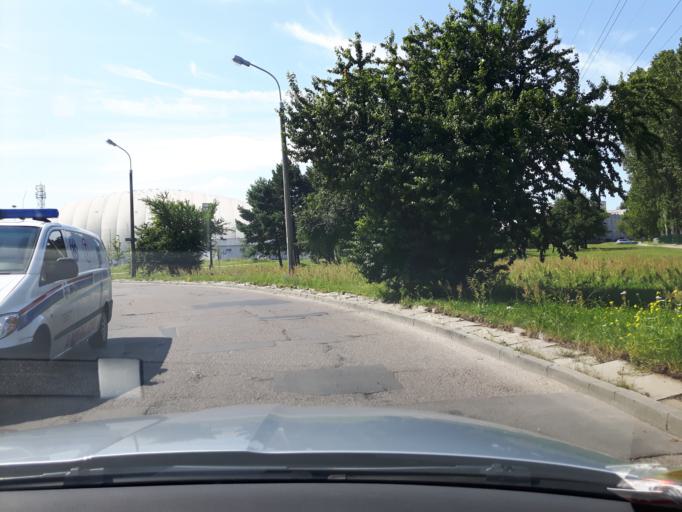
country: PL
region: Pomeranian Voivodeship
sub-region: Sopot
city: Sopot
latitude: 54.4025
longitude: 18.6031
